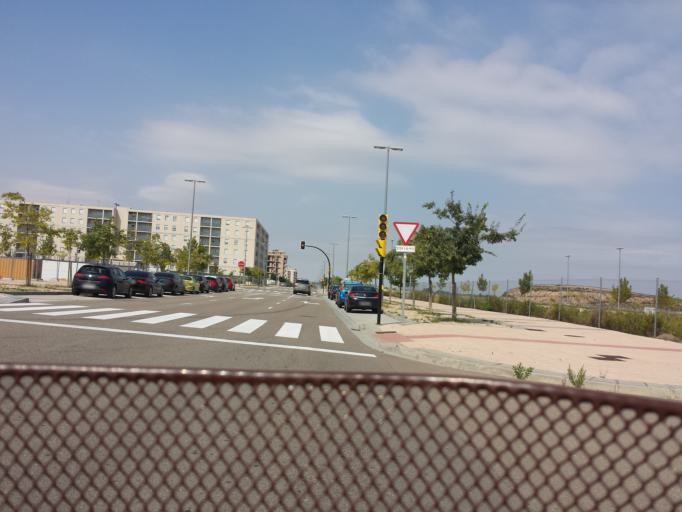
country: ES
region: Aragon
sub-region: Provincia de Zaragoza
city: Montecanal
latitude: 41.6260
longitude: -0.9560
